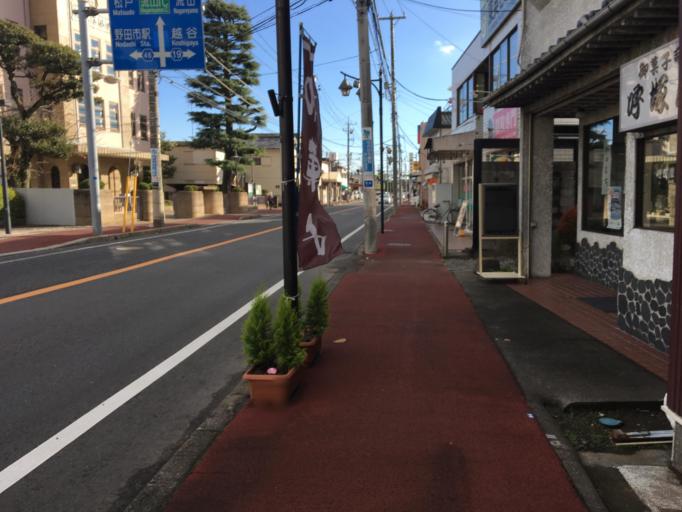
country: JP
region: Chiba
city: Noda
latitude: 35.9431
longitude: 139.8632
